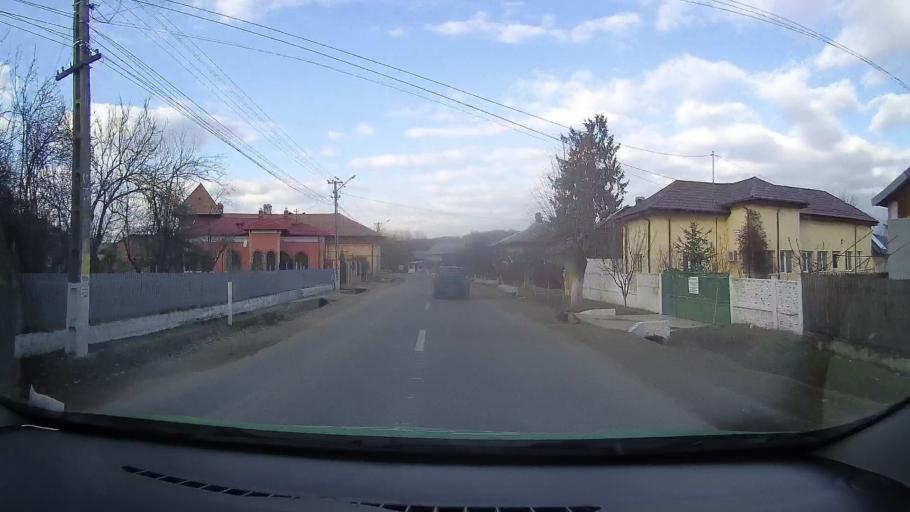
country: RO
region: Dambovita
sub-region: Comuna Gura Ocnitei
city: Gura Ocnitei
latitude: 44.9380
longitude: 25.5638
